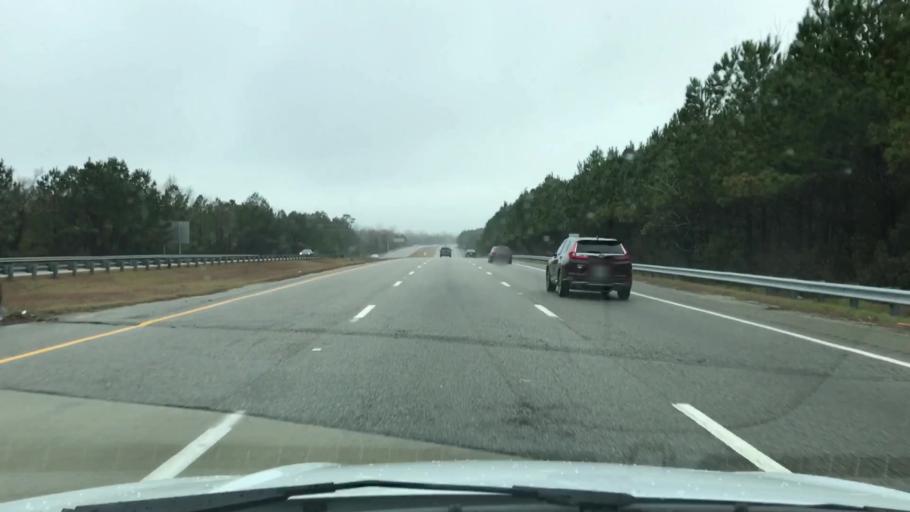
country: US
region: South Carolina
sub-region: Horry County
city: Myrtle Beach
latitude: 33.7508
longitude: -78.8688
